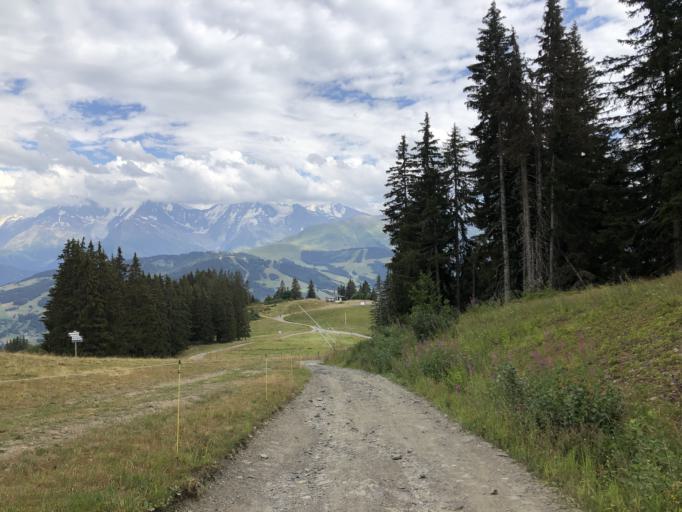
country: FR
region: Rhone-Alpes
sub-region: Departement de la Haute-Savoie
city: Megeve
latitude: 45.8780
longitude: 6.5902
